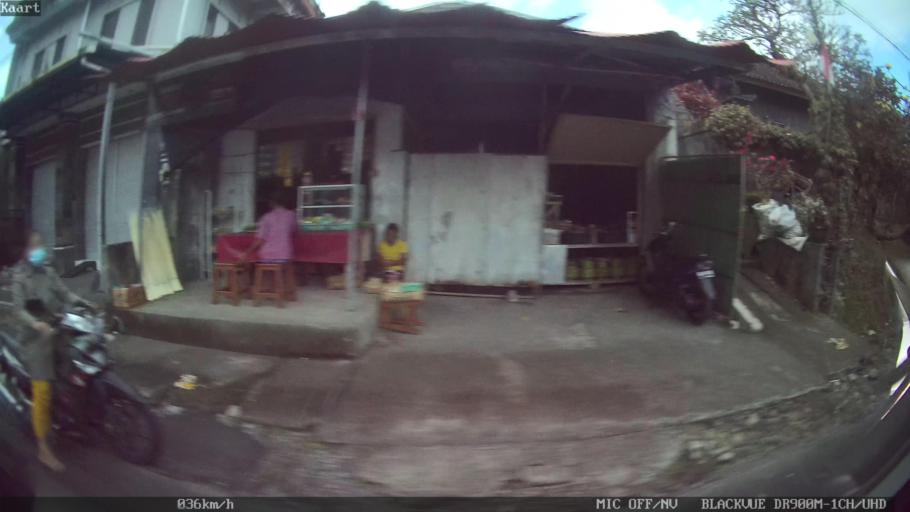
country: ID
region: Bali
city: Banjar Petak
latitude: -8.4472
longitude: 115.3190
